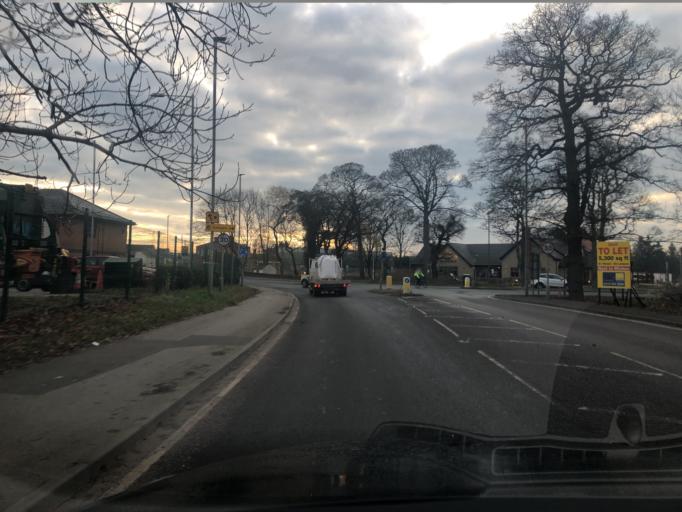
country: GB
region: England
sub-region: North Yorkshire
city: Northallerton
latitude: 54.3466
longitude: -1.4409
